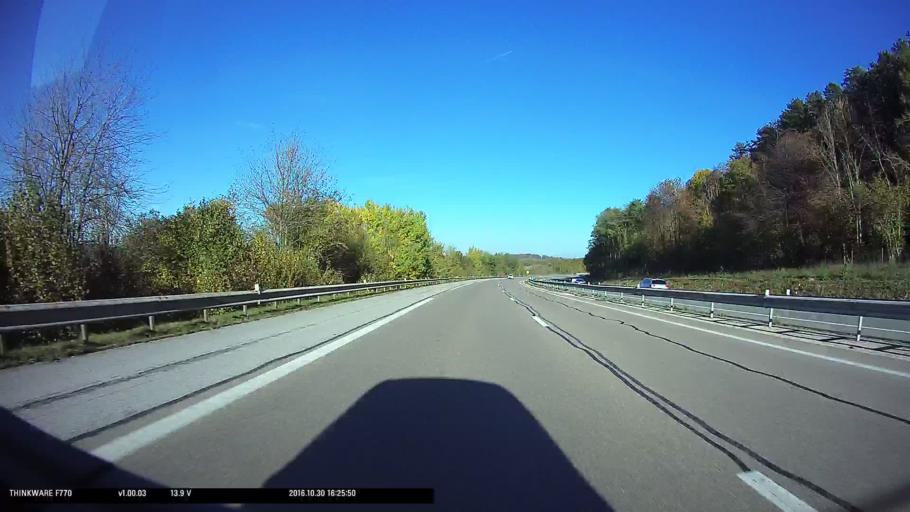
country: FR
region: Franche-Comte
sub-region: Departement du Doubs
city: Baume-les-Dames
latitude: 47.3713
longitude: 6.3378
